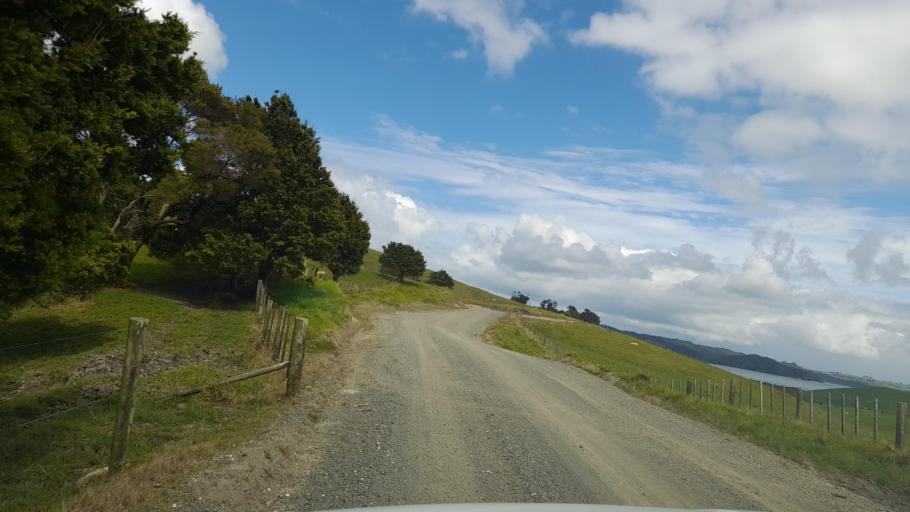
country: NZ
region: Auckland
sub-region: Auckland
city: Wellsford
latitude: -36.2113
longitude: 174.3289
